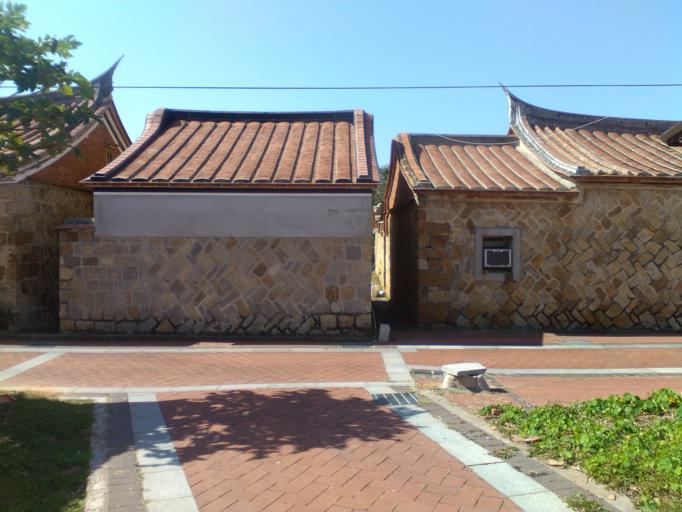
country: CN
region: Fujian
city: Shijing
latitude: 24.5045
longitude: 118.4419
